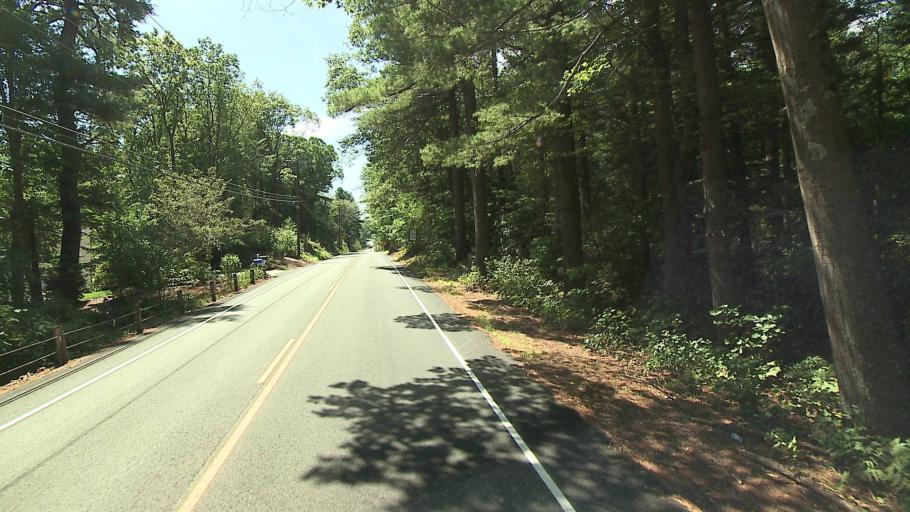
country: US
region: Connecticut
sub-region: Litchfield County
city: New Hartford Center
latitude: 41.9408
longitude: -72.9189
